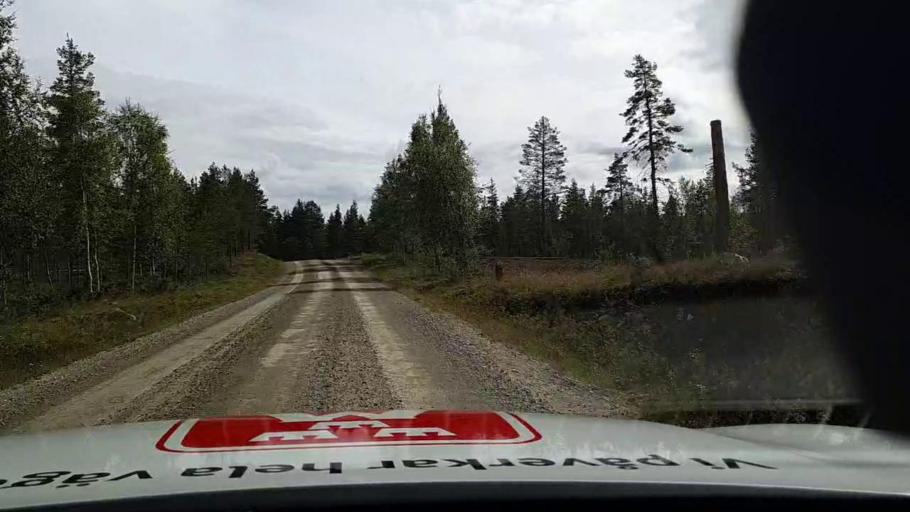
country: SE
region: Jaemtland
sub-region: Are Kommun
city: Jarpen
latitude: 62.5150
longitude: 13.4880
